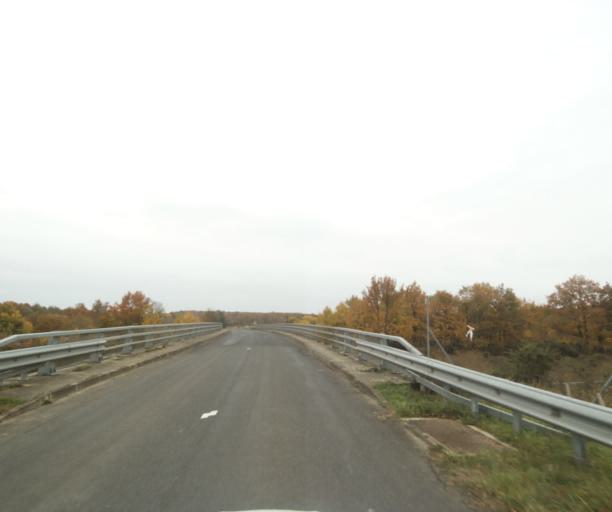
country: FR
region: Poitou-Charentes
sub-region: Departement de la Charente-Maritime
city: Chermignac
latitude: 45.7130
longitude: -0.6941
